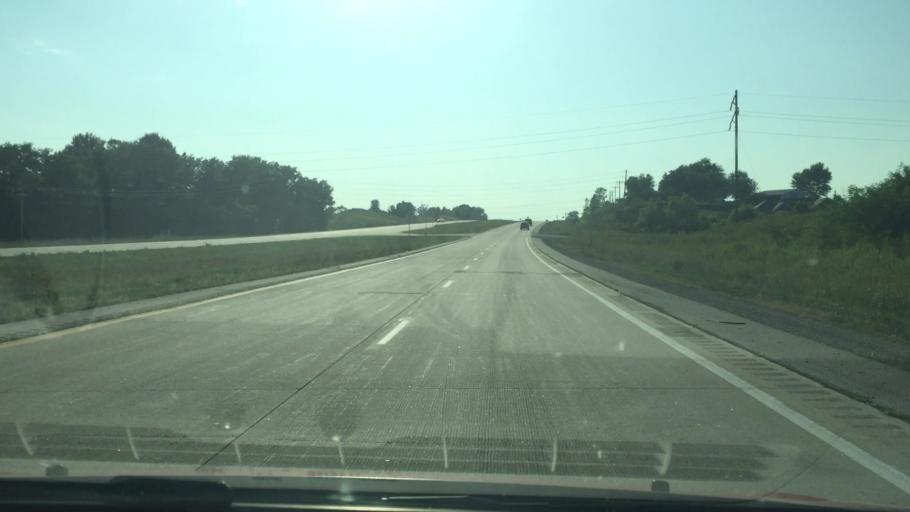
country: US
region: Iowa
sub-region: Scott County
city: Blue Grass
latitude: 41.5131
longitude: -90.8026
